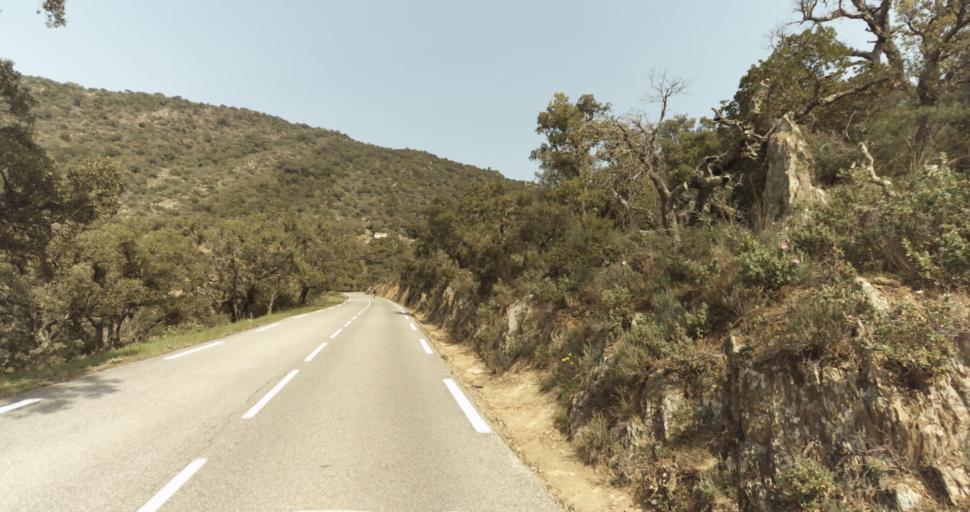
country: FR
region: Provence-Alpes-Cote d'Azur
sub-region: Departement du Var
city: Bormes-les-Mimosas
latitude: 43.1616
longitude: 6.3432
